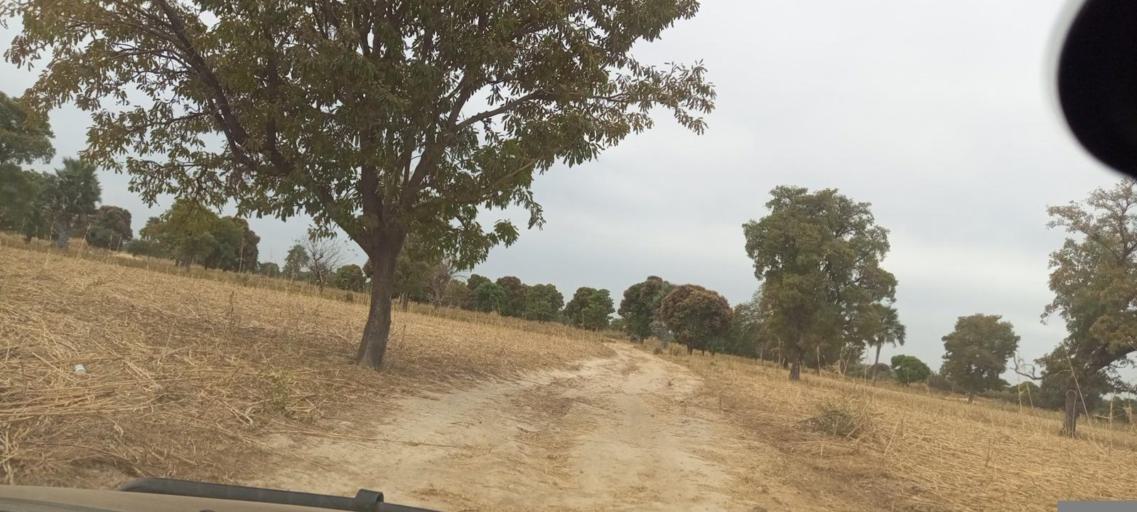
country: ML
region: Koulikoro
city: Kati
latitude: 12.7567
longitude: -8.3029
